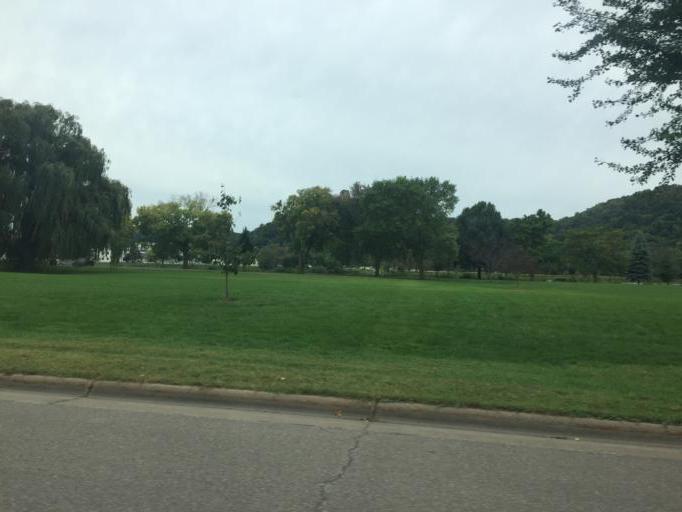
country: US
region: Minnesota
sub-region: Winona County
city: Winona
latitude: 44.0380
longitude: -91.6246
